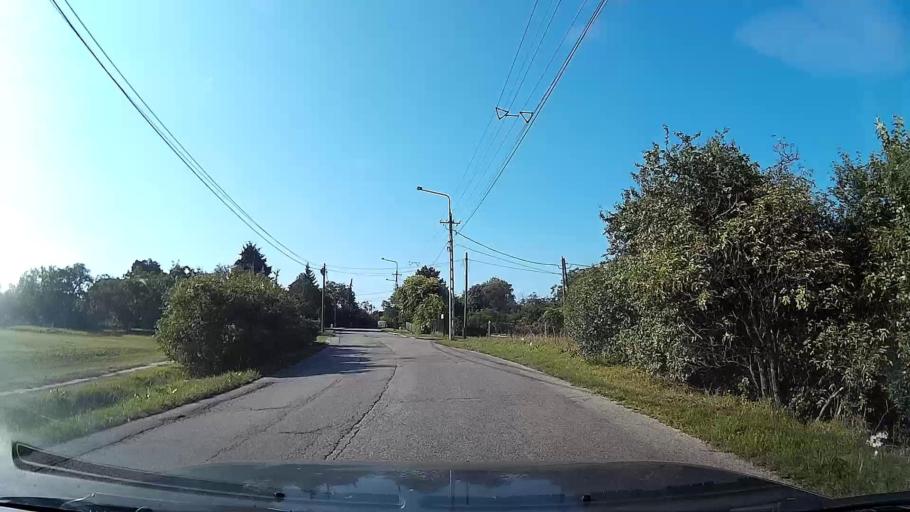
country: HU
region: Budapest
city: Budapest XXII. keruelet
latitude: 47.4229
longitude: 19.0047
